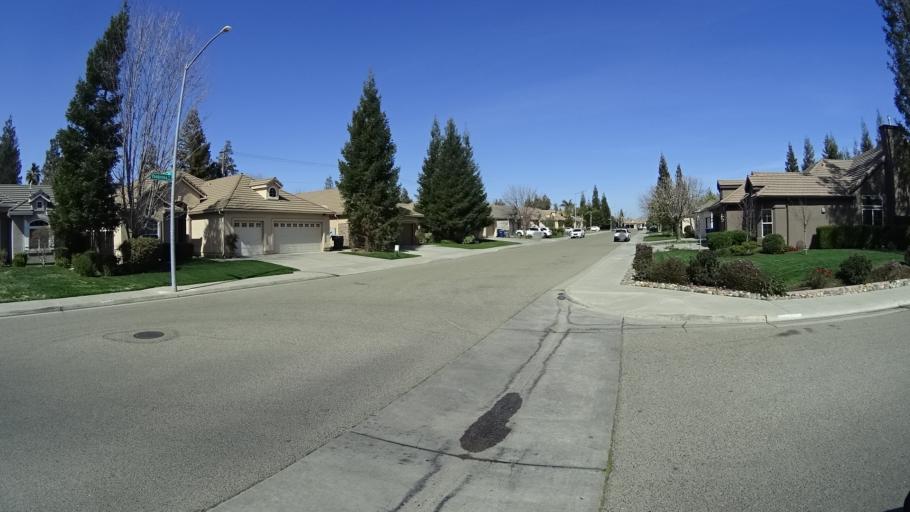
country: US
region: California
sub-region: Fresno County
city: Clovis
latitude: 36.8911
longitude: -119.7652
